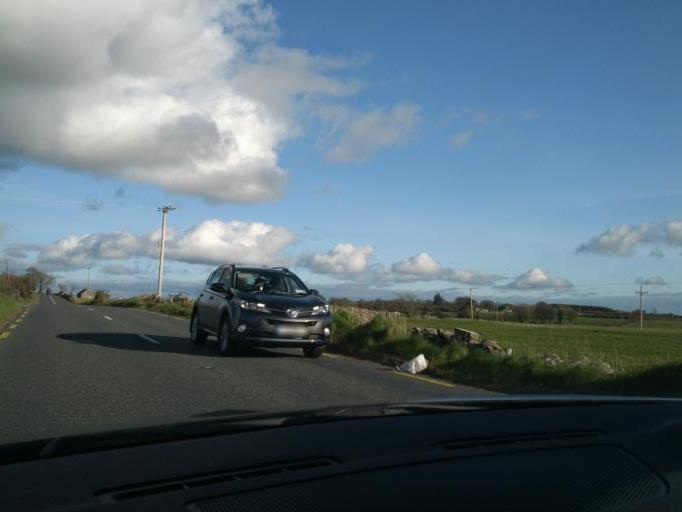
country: IE
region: Connaught
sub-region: Roscommon
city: Roscommon
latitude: 53.6672
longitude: -8.3115
